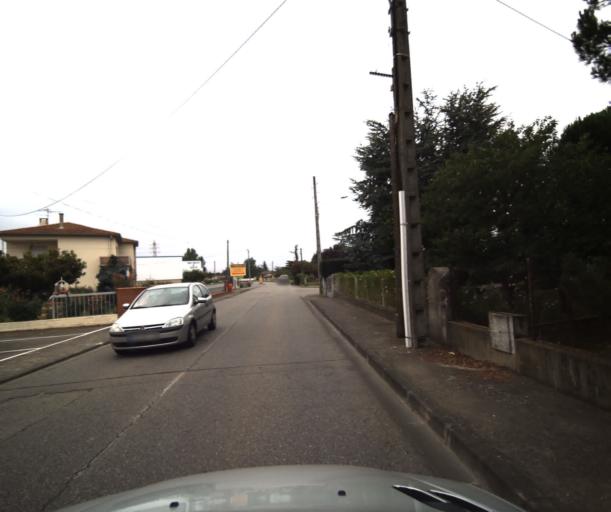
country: FR
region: Midi-Pyrenees
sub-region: Departement de la Haute-Garonne
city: Portet-sur-Garonne
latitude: 43.5348
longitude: 1.3986
